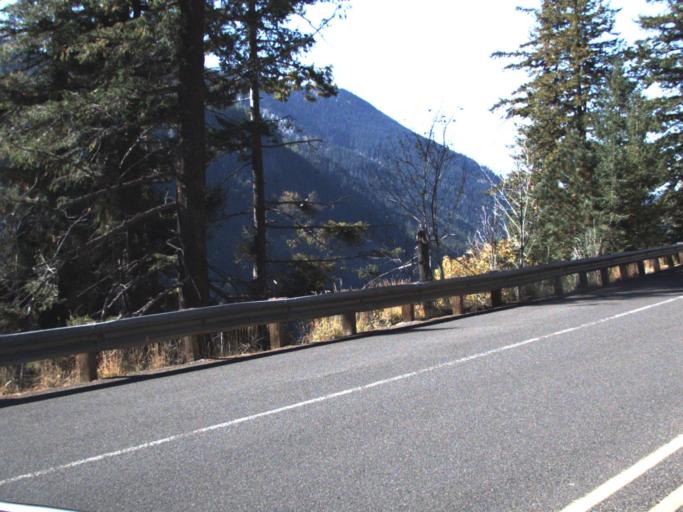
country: US
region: Washington
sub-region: Yakima County
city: Tieton
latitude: 46.6571
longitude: -121.3115
